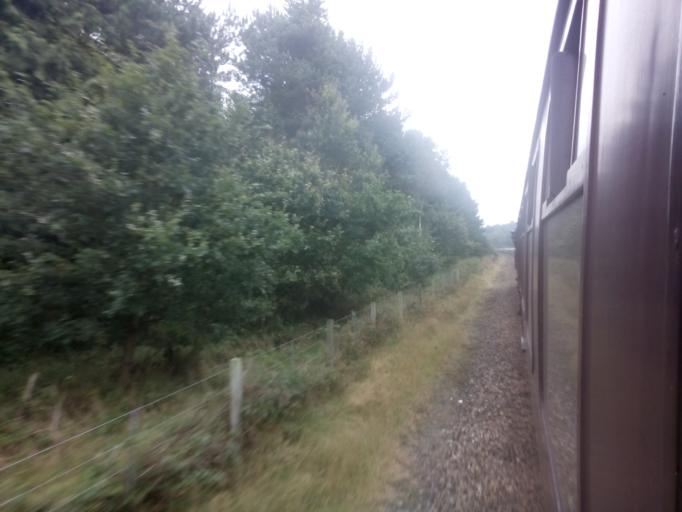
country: GB
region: England
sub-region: Norfolk
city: Sheringham
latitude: 52.9278
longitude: 1.1216
